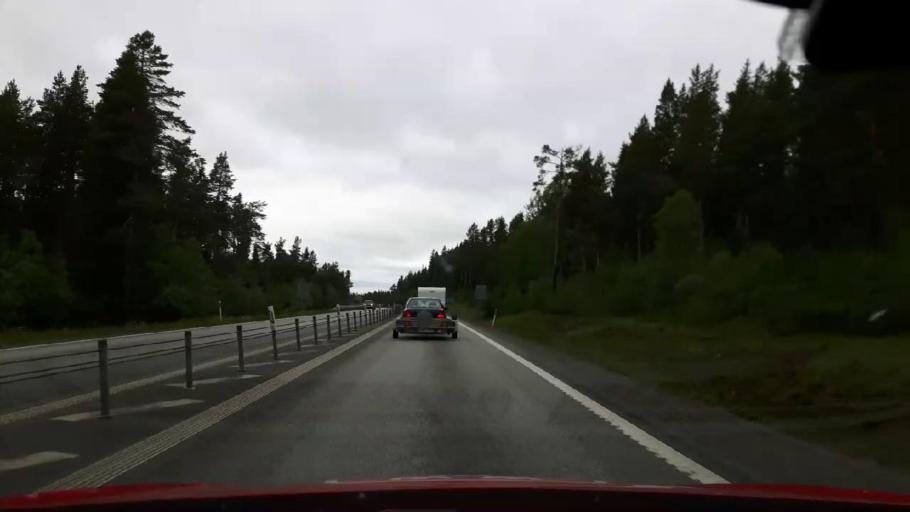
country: SE
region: Jaemtland
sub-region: OEstersunds Kommun
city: Ostersund
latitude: 63.1984
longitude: 14.6845
